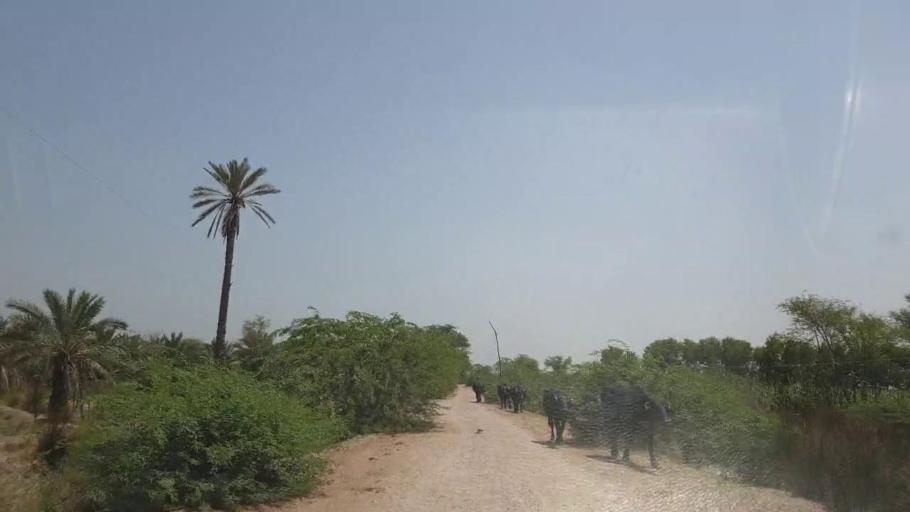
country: PK
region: Sindh
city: Kot Diji
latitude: 27.2879
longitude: 68.6435
